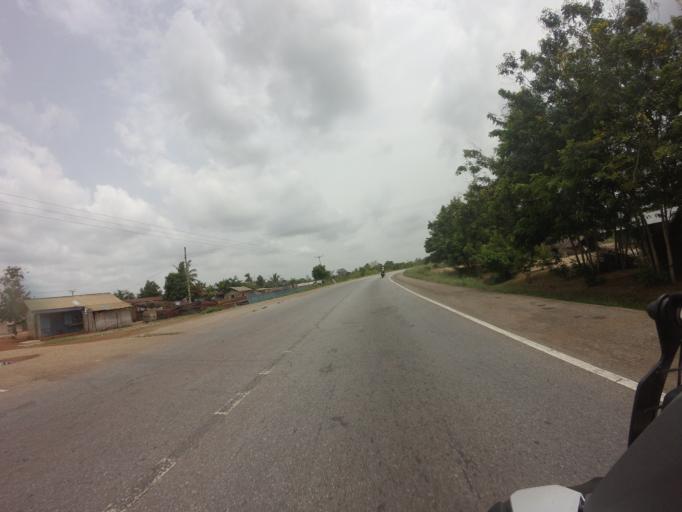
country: GH
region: Volta
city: Keta
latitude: 6.0866
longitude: 0.7421
